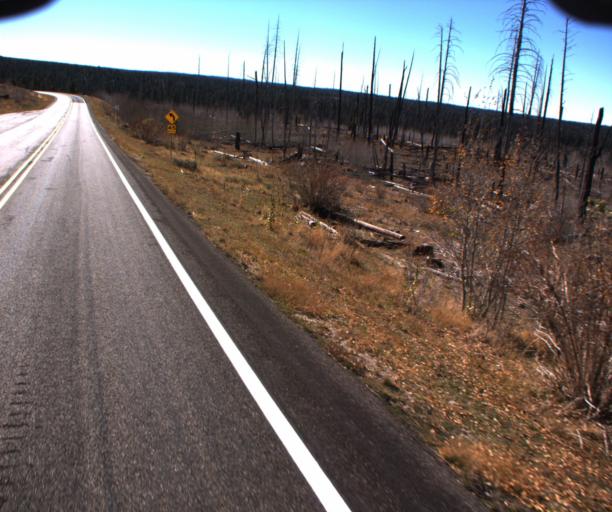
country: US
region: Arizona
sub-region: Coconino County
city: Grand Canyon
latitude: 36.5494
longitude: -112.1805
